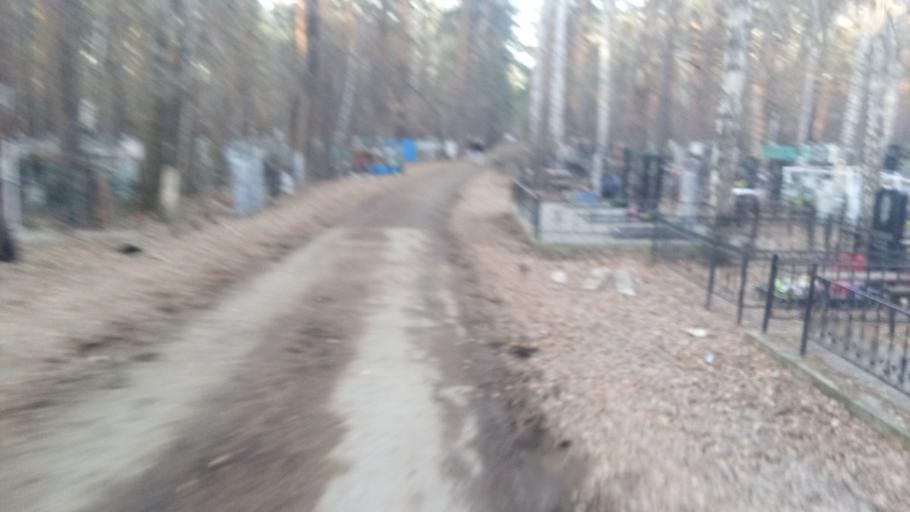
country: RU
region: Chelyabinsk
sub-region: Gorod Chelyabinsk
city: Chelyabinsk
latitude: 55.1286
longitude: 61.3489
